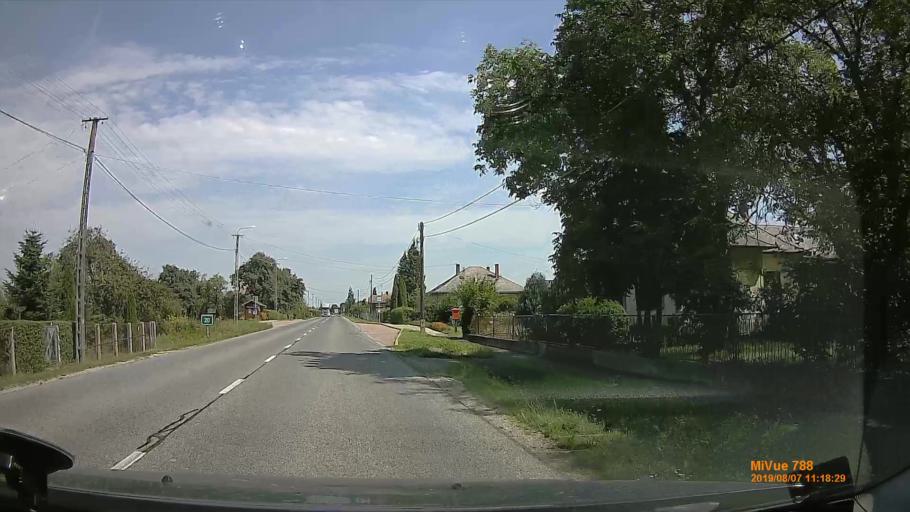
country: HU
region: Zala
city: Zalalovo
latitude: 46.7543
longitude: 16.5602
